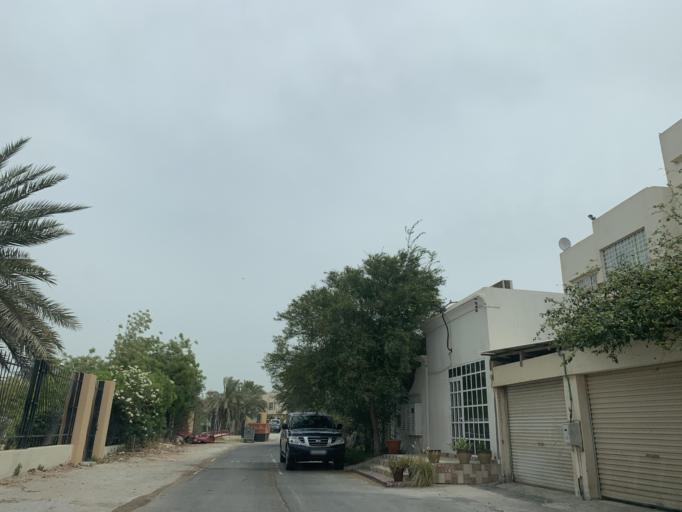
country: BH
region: Northern
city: Ar Rifa'
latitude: 26.1347
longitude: 50.5680
